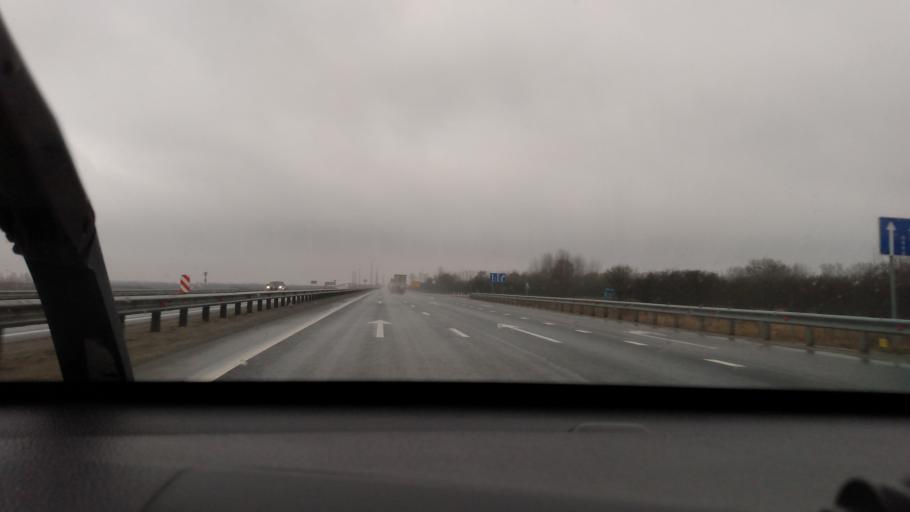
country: RU
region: Moskovskaya
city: Ozherel'ye
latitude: 54.7105
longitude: 38.1610
